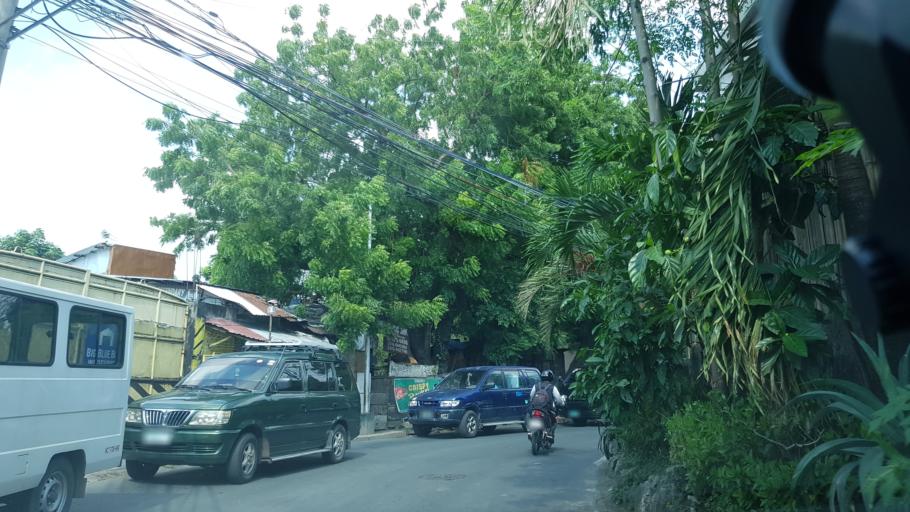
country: PH
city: Sambayanihan People's Village
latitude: 14.4727
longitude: 121.0227
